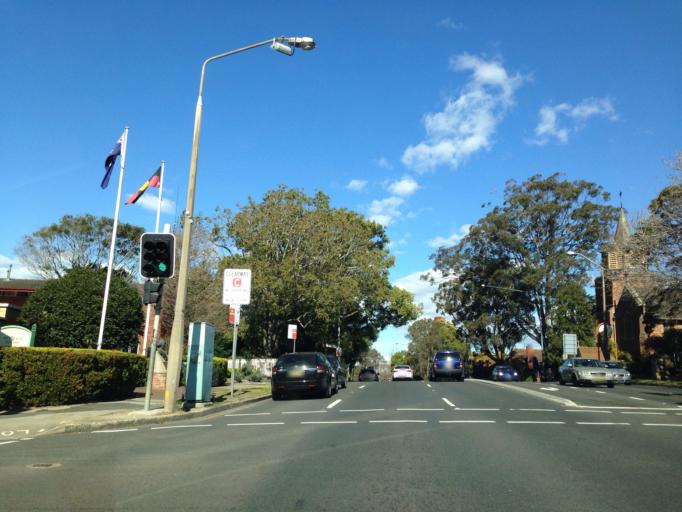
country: AU
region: New South Wales
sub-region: Ku-ring-gai
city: Killara
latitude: -33.7565
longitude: 151.1531
